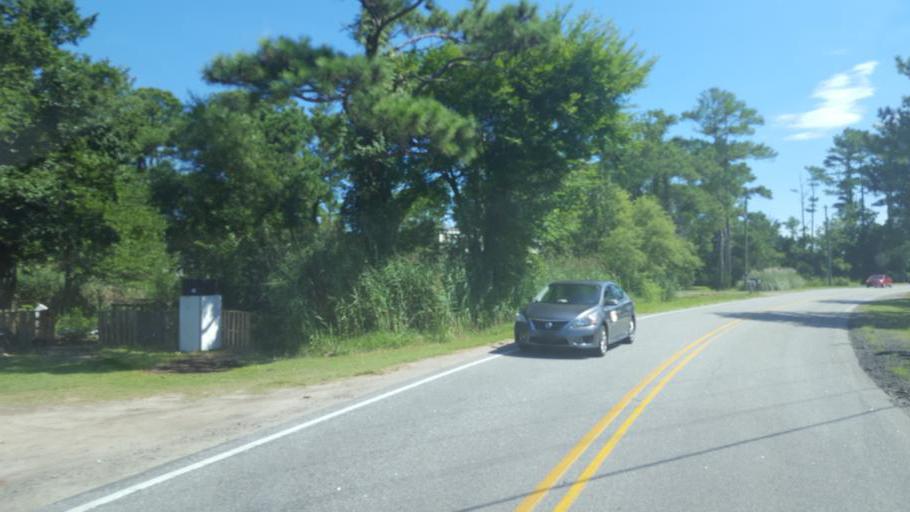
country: US
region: North Carolina
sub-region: Dare County
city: Kill Devil Hills
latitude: 36.0154
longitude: -75.6932
